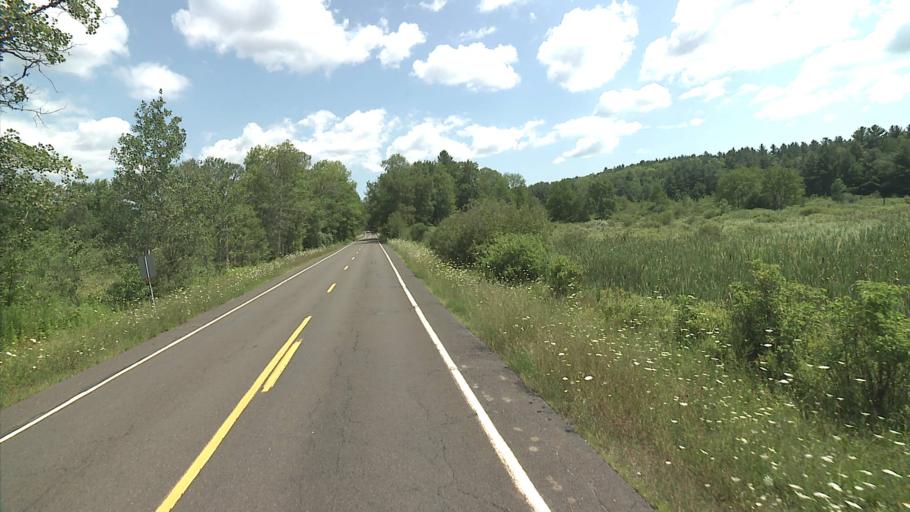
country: US
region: Connecticut
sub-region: Litchfield County
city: Winsted
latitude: 41.9890
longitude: -73.1014
